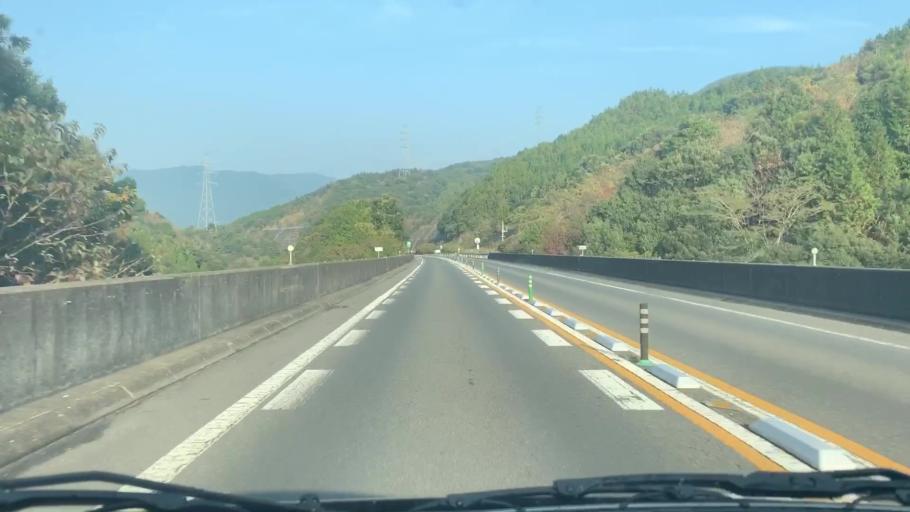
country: JP
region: Saga Prefecture
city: Imaricho-ko
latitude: 33.1622
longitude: 129.8644
